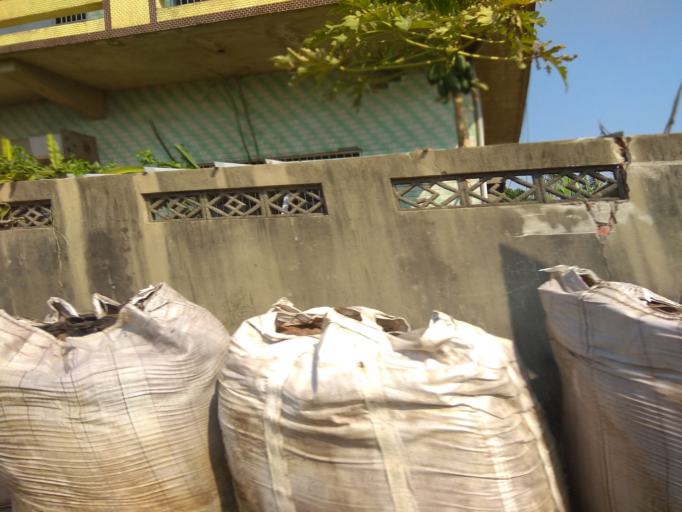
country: TW
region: Taiwan
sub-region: Hsinchu
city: Zhubei
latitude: 24.9945
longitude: 121.0660
